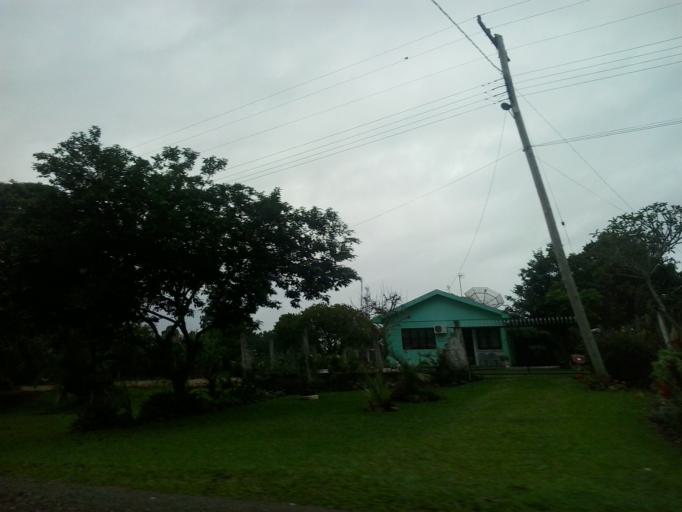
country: BR
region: Rio Grande do Sul
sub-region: Santa Maria
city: Santa Maria
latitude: -29.7222
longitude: -53.3740
